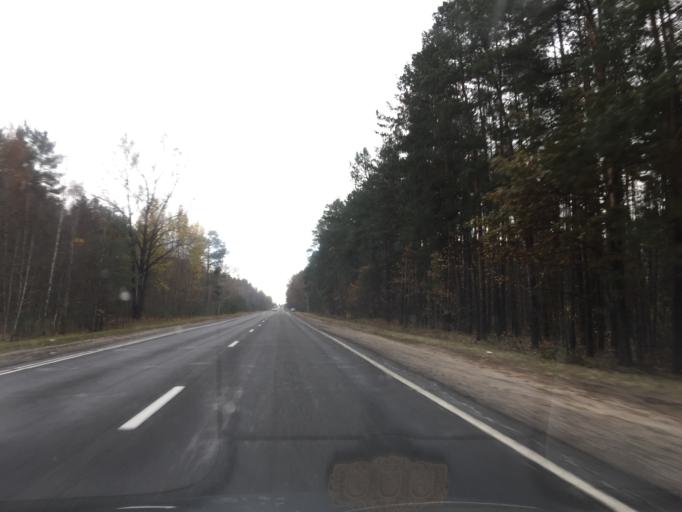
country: BY
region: Gomel
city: Gomel
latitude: 52.4043
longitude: 30.8291
